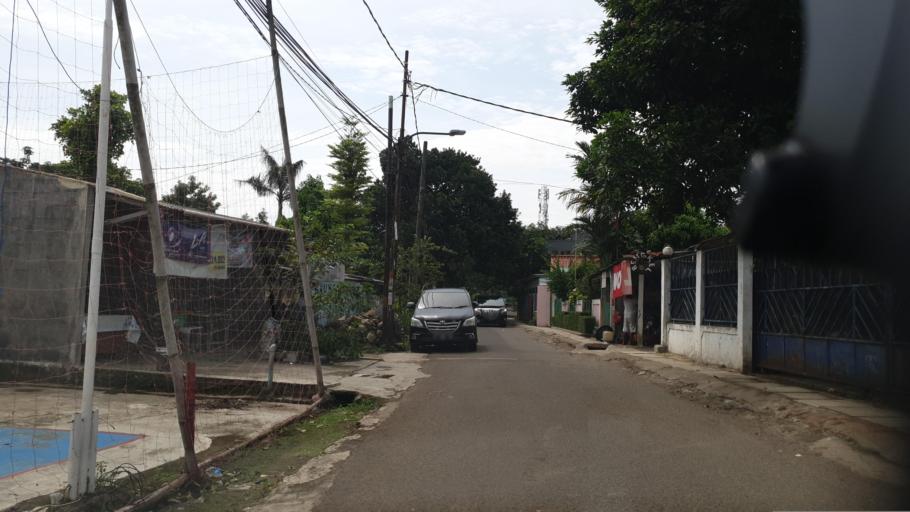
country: ID
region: West Java
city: Pamulang
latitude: -6.3493
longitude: 106.7669
